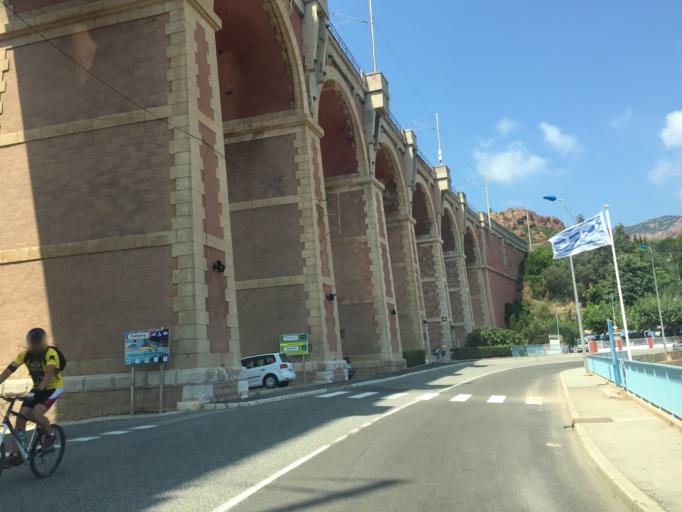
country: FR
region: Provence-Alpes-Cote d'Azur
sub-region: Departement des Alpes-Maritimes
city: Theoule-sur-Mer
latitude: 43.4372
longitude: 6.8921
